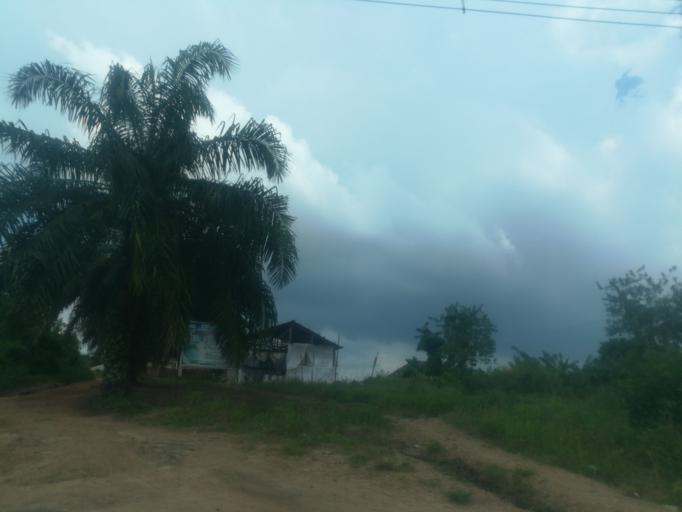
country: NG
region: Oyo
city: Ido
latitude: 7.4113
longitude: 3.8217
